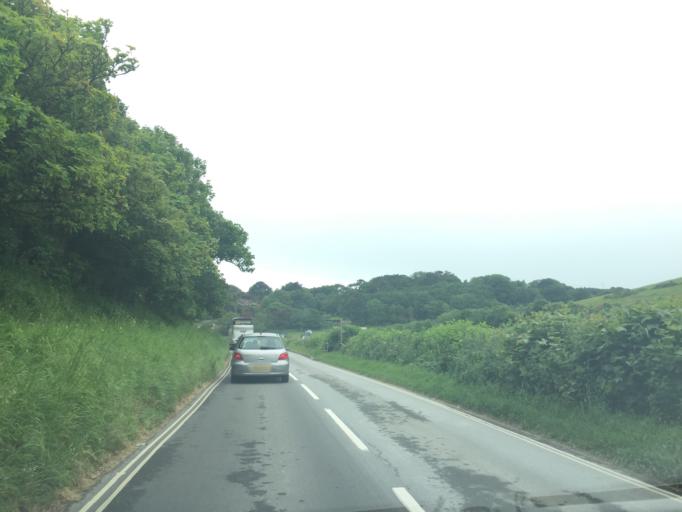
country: GB
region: England
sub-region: Dorset
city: Wool
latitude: 50.6227
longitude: -2.2527
